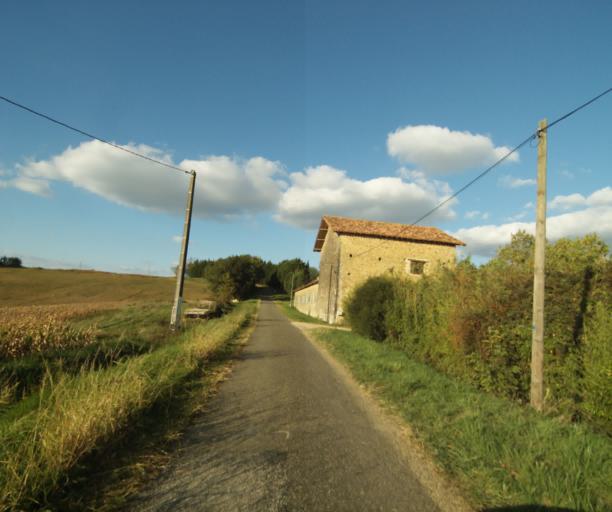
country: FR
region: Midi-Pyrenees
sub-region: Departement du Gers
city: Eauze
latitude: 43.7463
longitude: 0.1192
